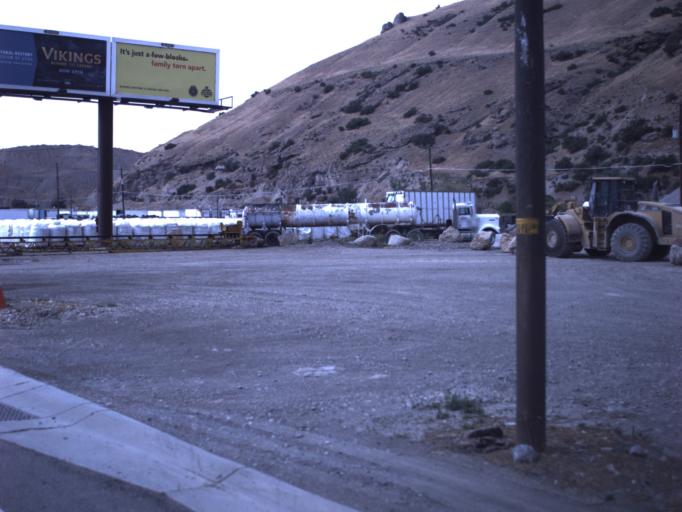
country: US
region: Utah
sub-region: Salt Lake County
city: Salt Lake City
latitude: 40.7968
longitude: -111.9064
